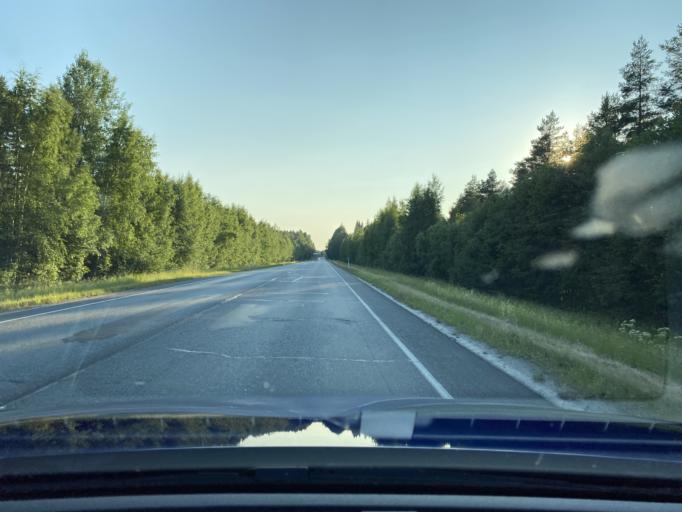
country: FI
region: Haeme
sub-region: Forssa
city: Tammela
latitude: 60.8262
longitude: 23.9475
